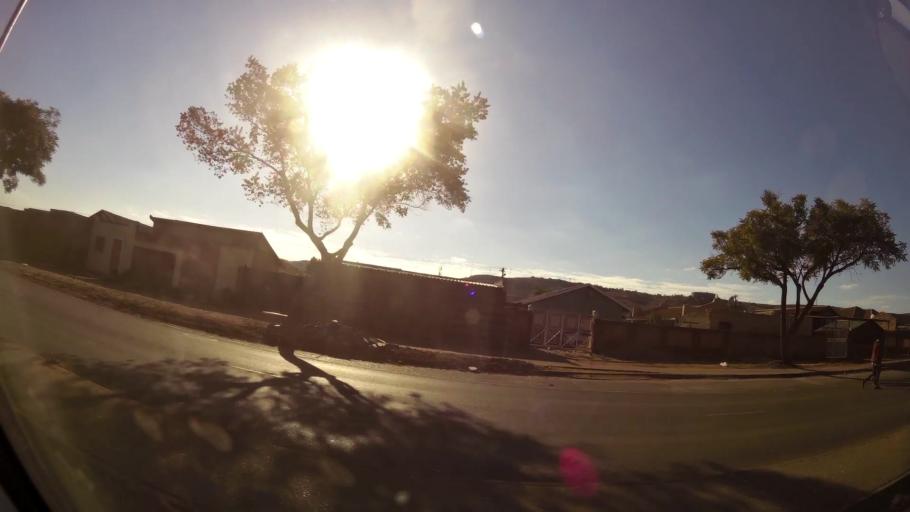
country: ZA
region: Gauteng
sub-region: City of Tshwane Metropolitan Municipality
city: Cullinan
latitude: -25.7087
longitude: 28.3842
